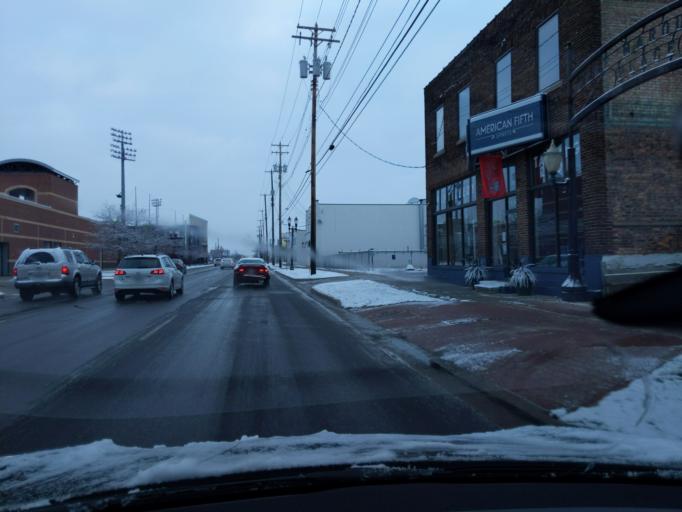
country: US
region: Michigan
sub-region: Ingham County
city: Lansing
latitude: 42.7339
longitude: -84.5446
